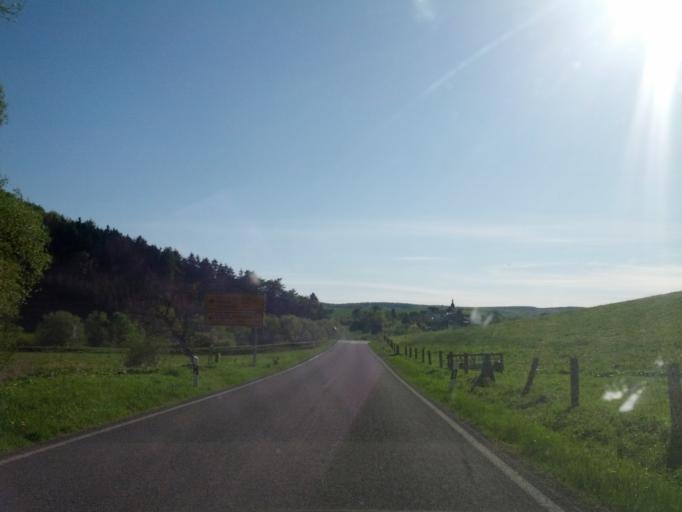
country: DE
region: Thuringia
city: Schwobfeld
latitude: 51.2715
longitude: 10.1175
